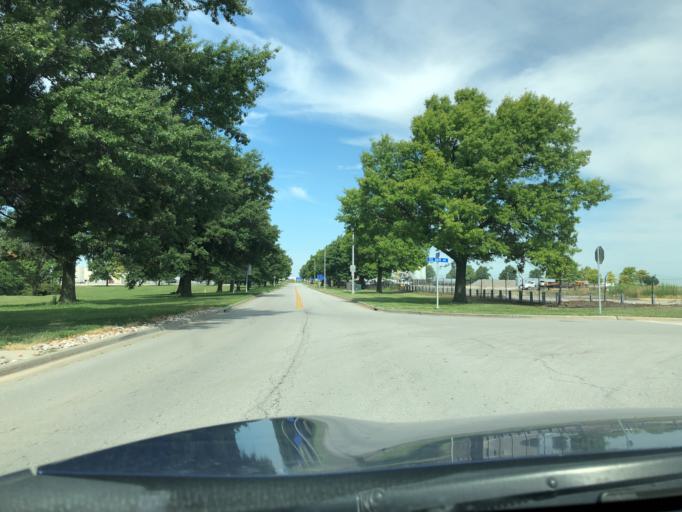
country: US
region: Missouri
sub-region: Platte County
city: Weatherby Lake
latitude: 39.3120
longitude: -94.7119
